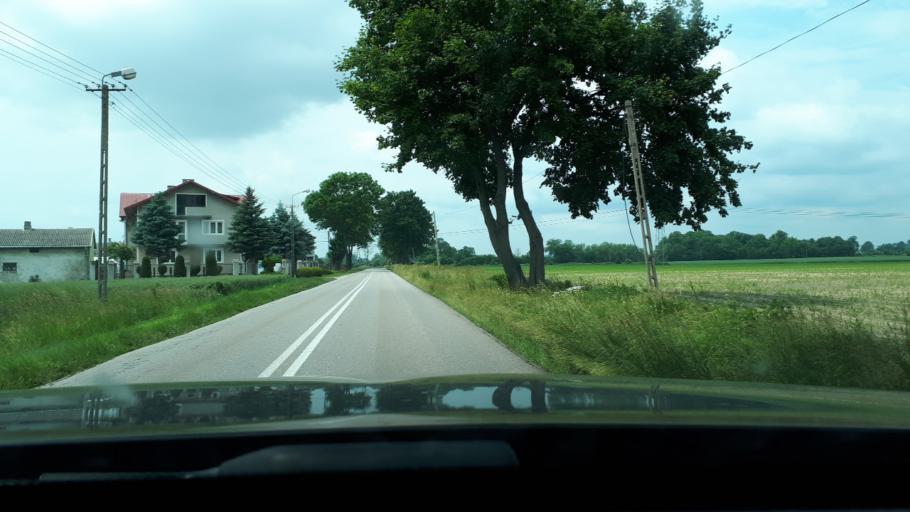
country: PL
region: Masovian Voivodeship
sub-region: Powiat warszawski zachodni
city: Blonie
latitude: 52.2373
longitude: 20.6556
